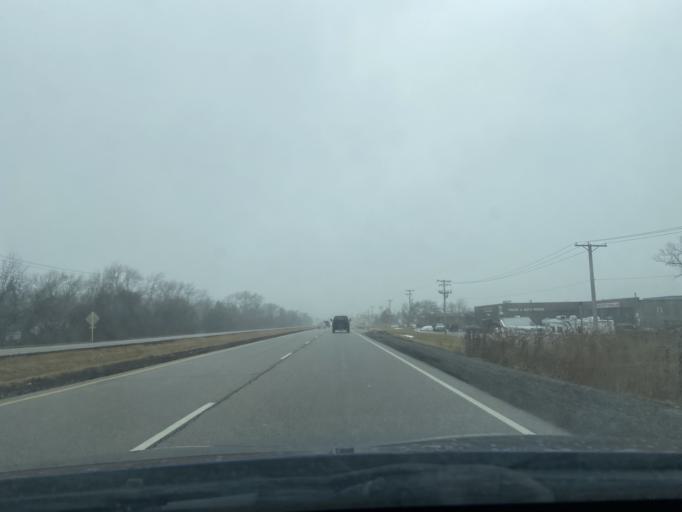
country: US
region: Illinois
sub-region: Lake County
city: Wauconda
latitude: 42.2719
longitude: -88.1545
